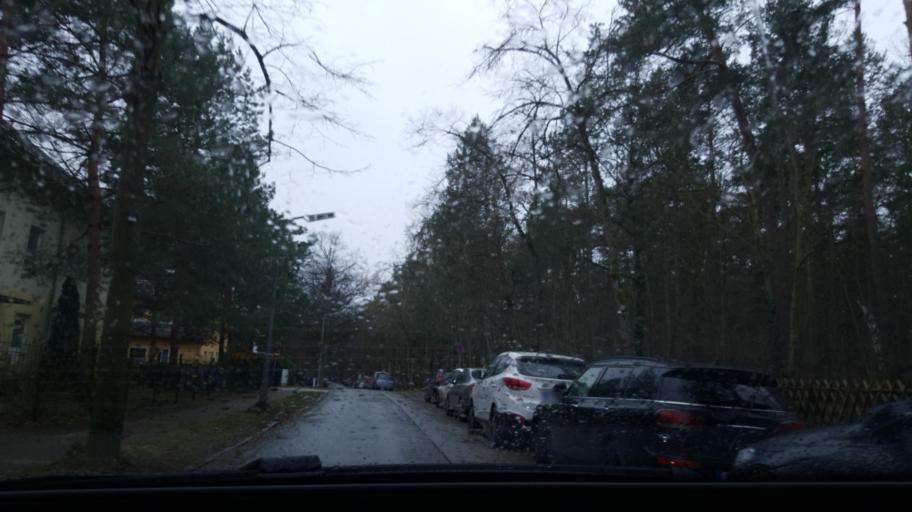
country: DE
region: Berlin
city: Wannsee
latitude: 52.4319
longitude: 13.1624
